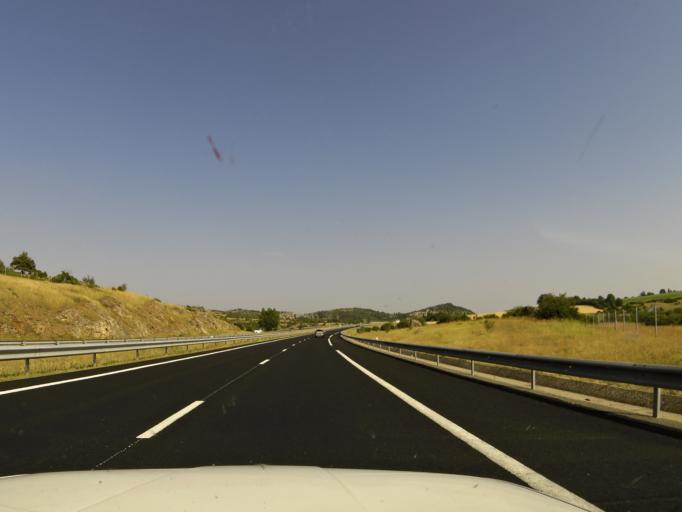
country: FR
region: Midi-Pyrenees
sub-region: Departement de l'Aveyron
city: La Cavalerie
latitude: 43.9058
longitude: 3.2719
